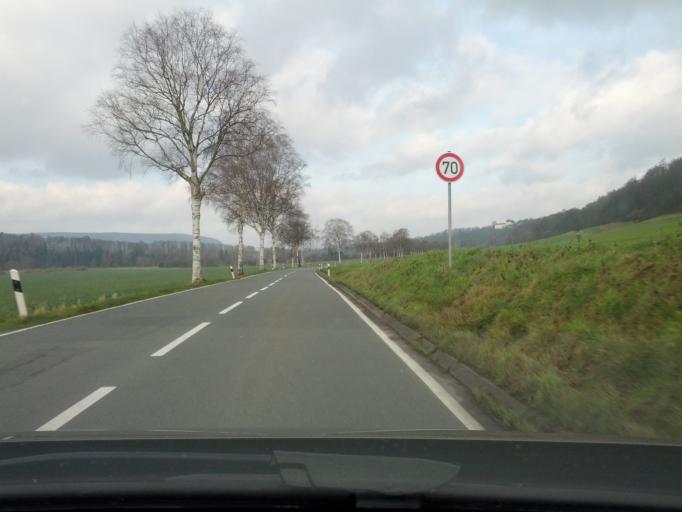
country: DE
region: Lower Saxony
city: Furstenberg
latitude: 51.7139
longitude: 9.3936
